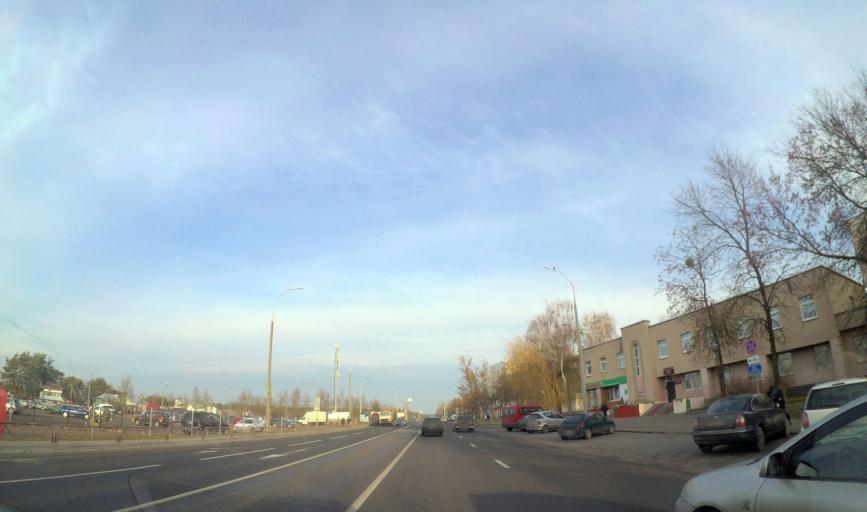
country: BY
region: Grodnenskaya
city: Hrodna
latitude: 53.6682
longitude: 23.7895
